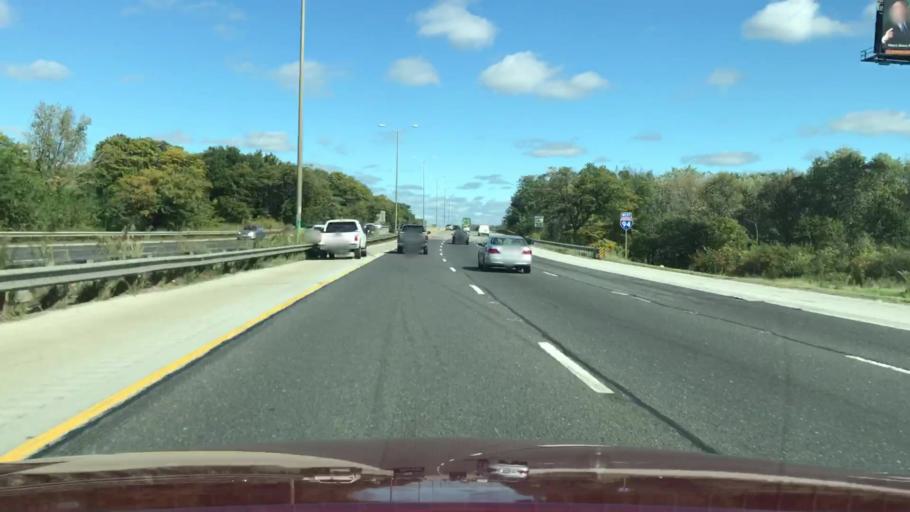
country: US
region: Illinois
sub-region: Cook County
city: South Holland
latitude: 41.6052
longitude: -87.5828
